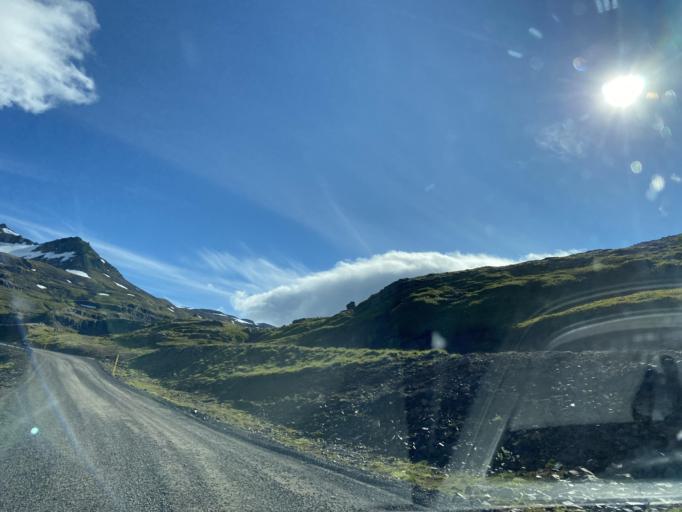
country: IS
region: East
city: Eskifjoerdur
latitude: 65.1804
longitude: -14.0875
